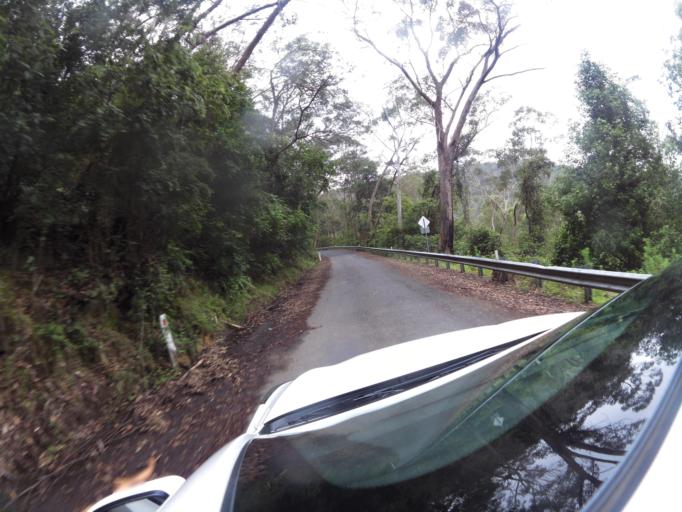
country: AU
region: New South Wales
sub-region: Hawkesbury
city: Pitt Town
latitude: -33.4315
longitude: 150.9443
